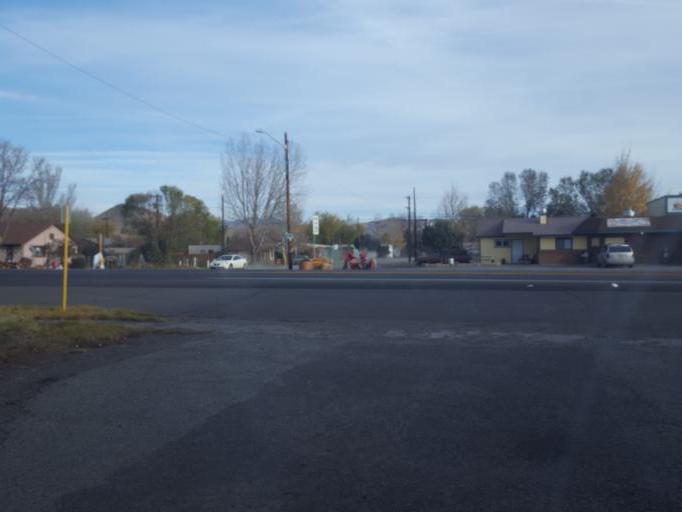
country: US
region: Colorado
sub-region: Rio Grande County
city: Del Norte
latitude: 37.6789
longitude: -106.3572
